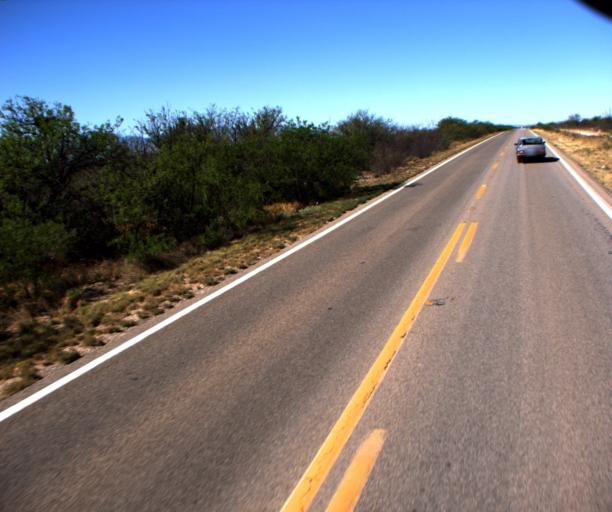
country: US
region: Arizona
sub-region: Cochise County
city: Huachuca City
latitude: 31.7067
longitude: -110.2849
